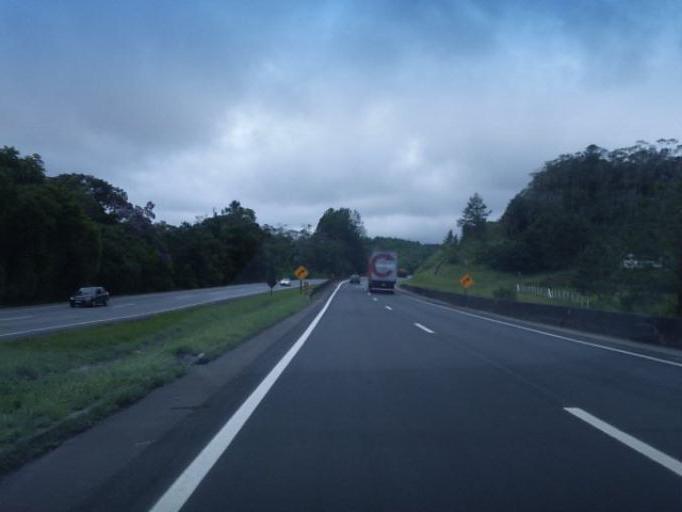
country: BR
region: Parana
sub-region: Antonina
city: Antonina
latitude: -25.1025
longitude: -48.6999
